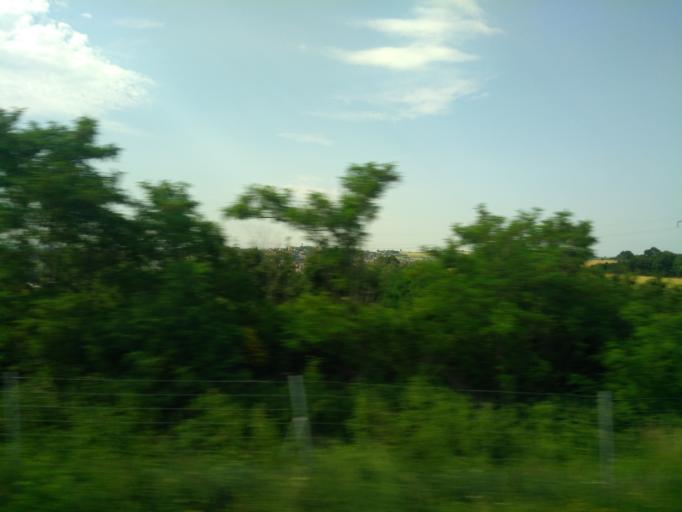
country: FR
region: Rhone-Alpes
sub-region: Departement du Rhone
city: Communay
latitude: 45.5909
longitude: 4.8375
